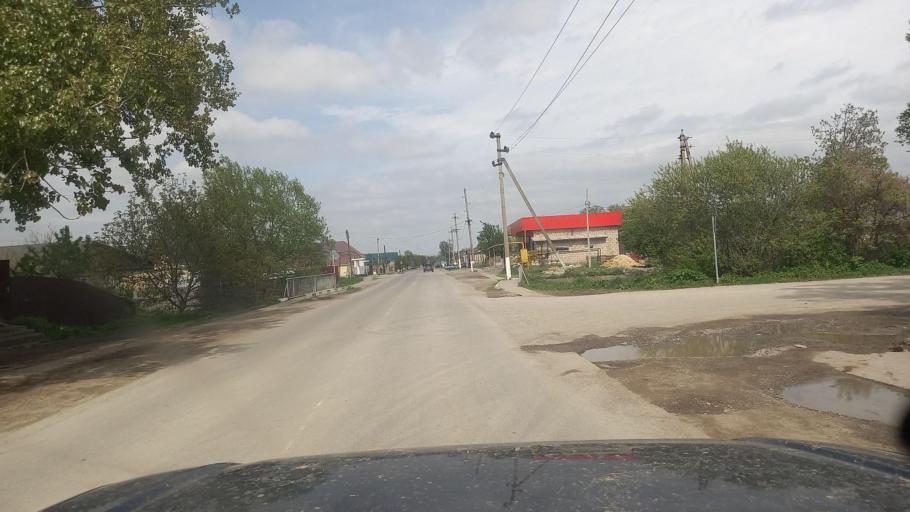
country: RU
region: Kabardino-Balkariya
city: Sarmakovo
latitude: 43.7357
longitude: 43.1785
